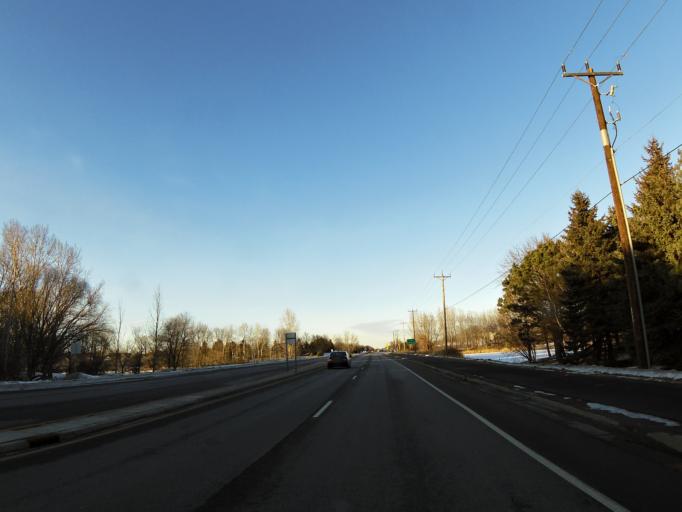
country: US
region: Minnesota
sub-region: Washington County
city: Woodbury
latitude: 44.8995
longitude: -92.9034
